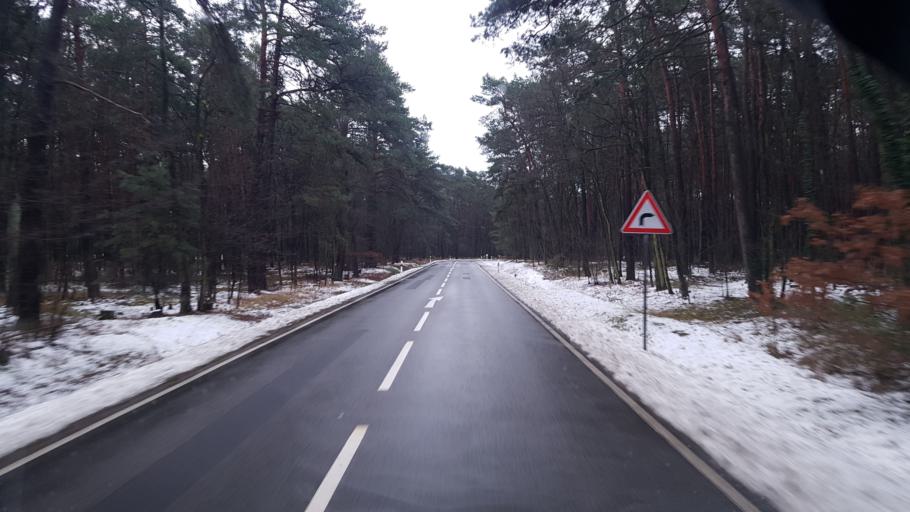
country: DE
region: Brandenburg
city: Schenkendobern
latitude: 51.9042
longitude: 14.6341
